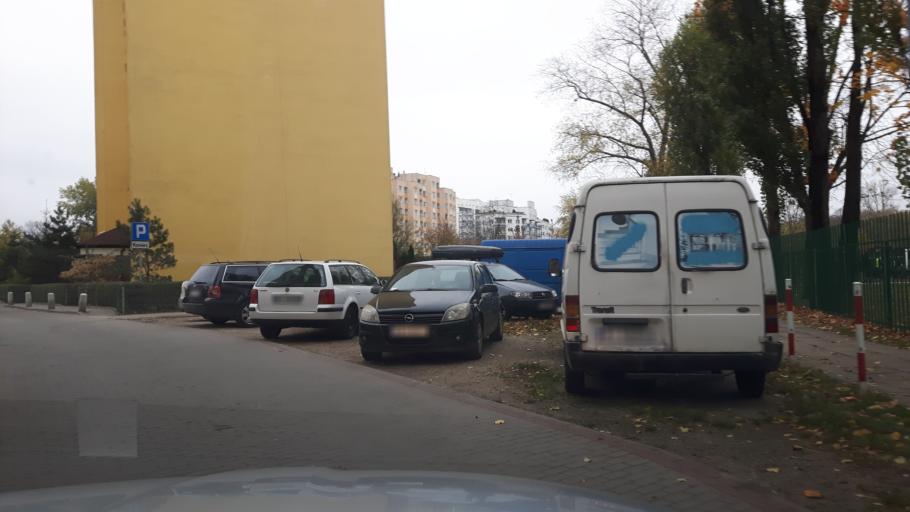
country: PL
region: Masovian Voivodeship
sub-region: Warszawa
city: Targowek
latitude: 52.2747
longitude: 21.0457
